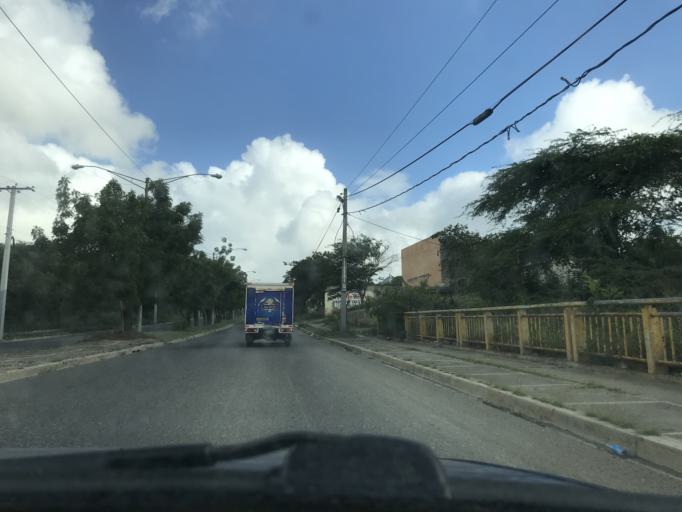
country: DO
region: Santiago
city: Santiago de los Caballeros
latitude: 19.4148
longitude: -70.7296
